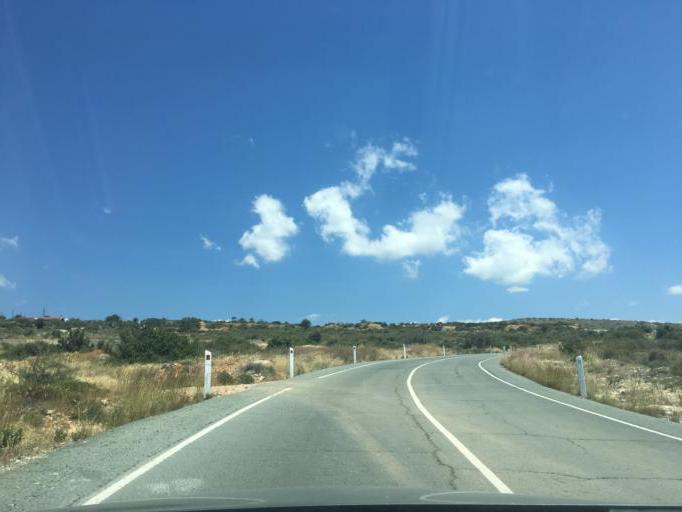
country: CY
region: Limassol
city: Mouttagiaka
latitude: 34.7408
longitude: 33.0624
